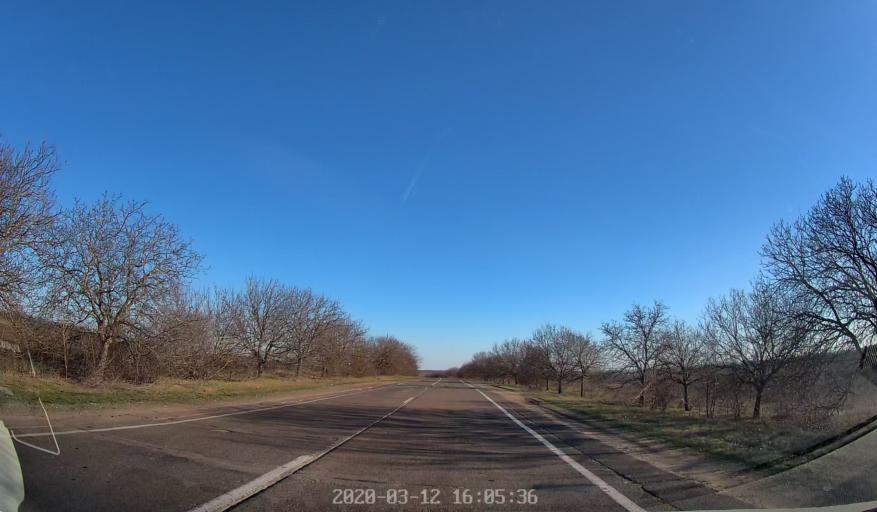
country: MD
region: Anenii Noi
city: Anenii Noi
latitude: 47.0023
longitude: 29.1806
